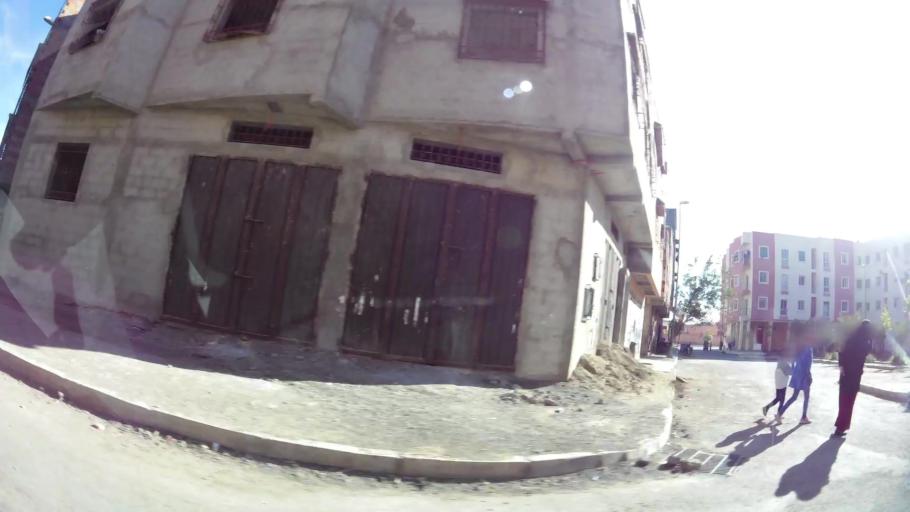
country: MA
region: Marrakech-Tensift-Al Haouz
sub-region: Marrakech
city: Marrakesh
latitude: 31.6885
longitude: -8.0704
